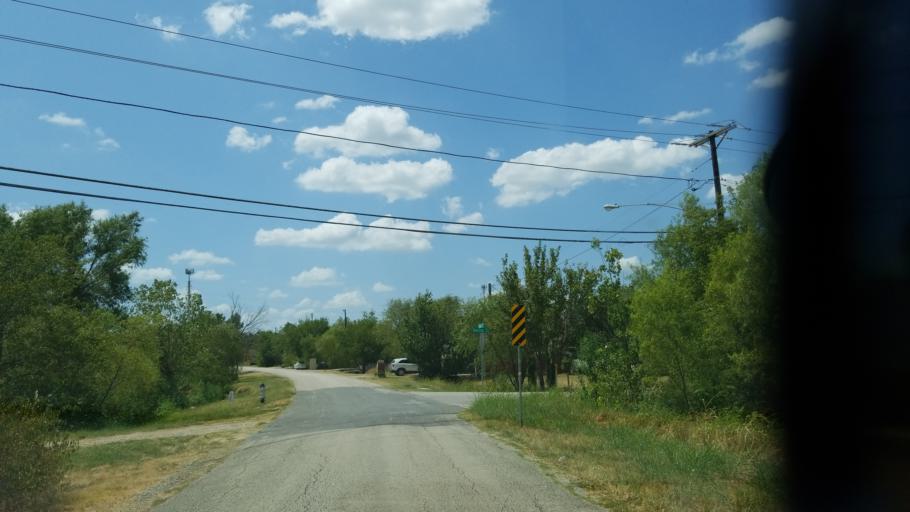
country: US
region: Texas
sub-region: Dallas County
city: Cockrell Hill
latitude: 32.7451
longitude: -96.9203
